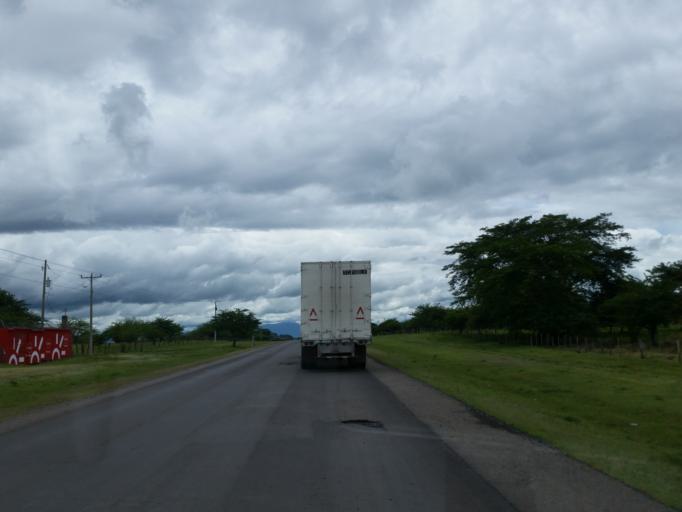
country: NI
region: Chinandega
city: Somotillo
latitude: 12.9081
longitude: -86.8516
